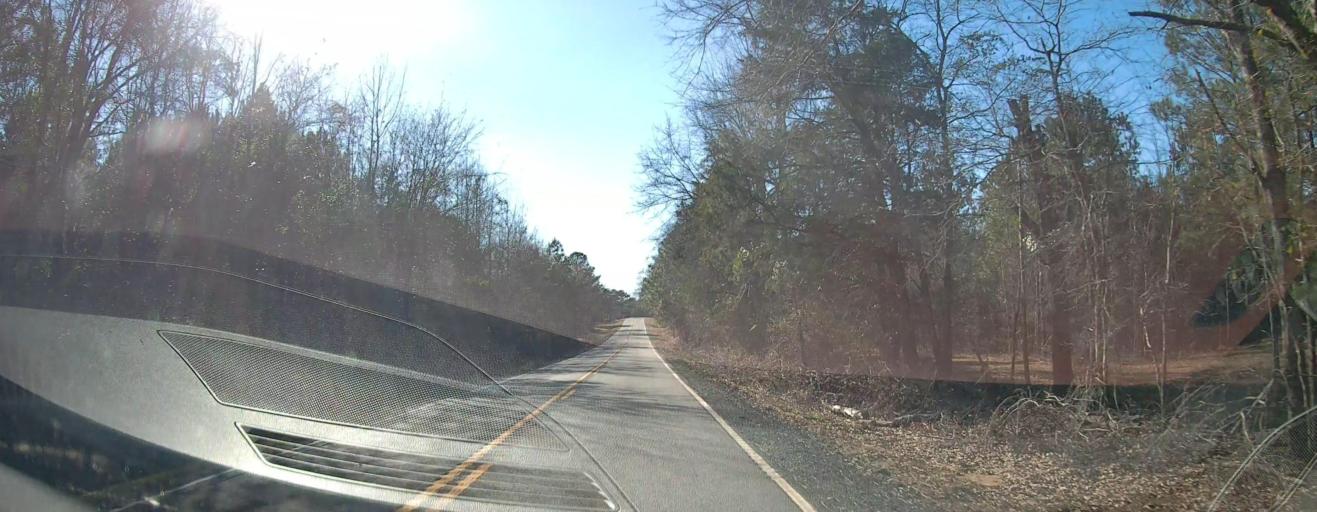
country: US
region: Georgia
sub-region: Taylor County
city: Butler
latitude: 32.6463
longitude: -84.3761
